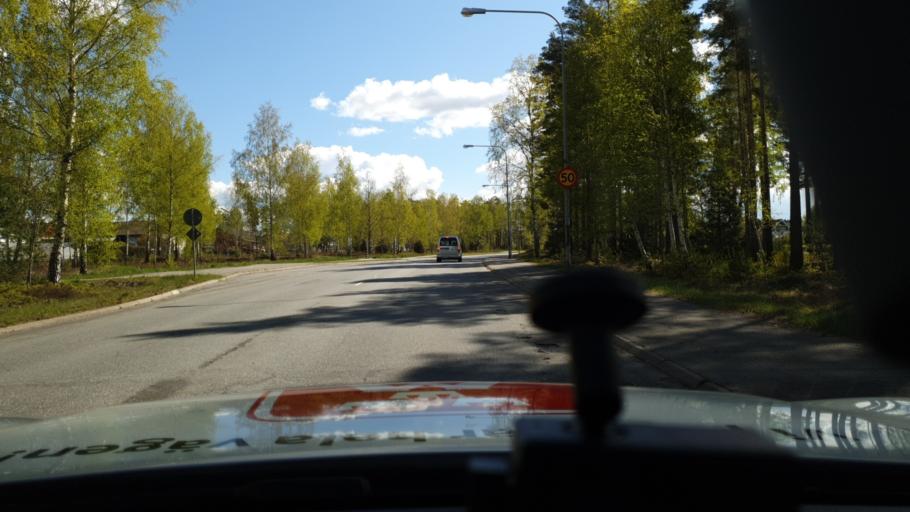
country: SE
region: Kalmar
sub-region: Vimmerby Kommun
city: Vimmerby
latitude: 57.6793
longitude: 15.8554
